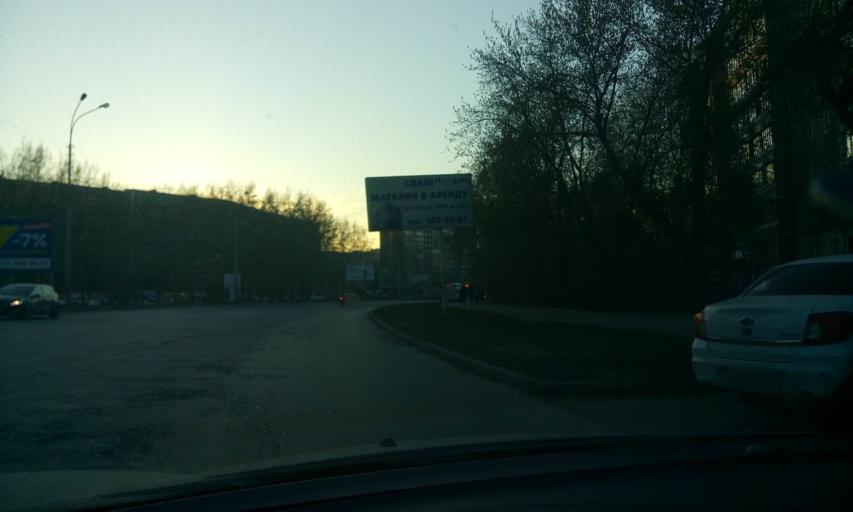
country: RU
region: Sverdlovsk
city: Yekaterinburg
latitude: 56.8357
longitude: 60.6821
